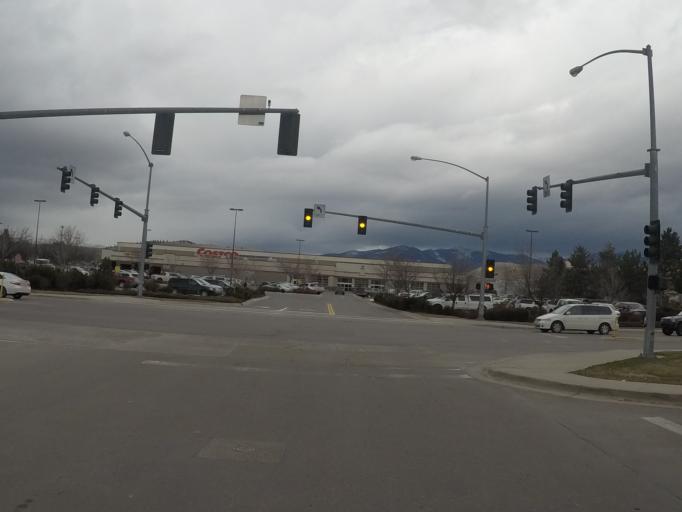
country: US
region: Montana
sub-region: Missoula County
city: Orchard Homes
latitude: 46.8937
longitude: -114.0375
